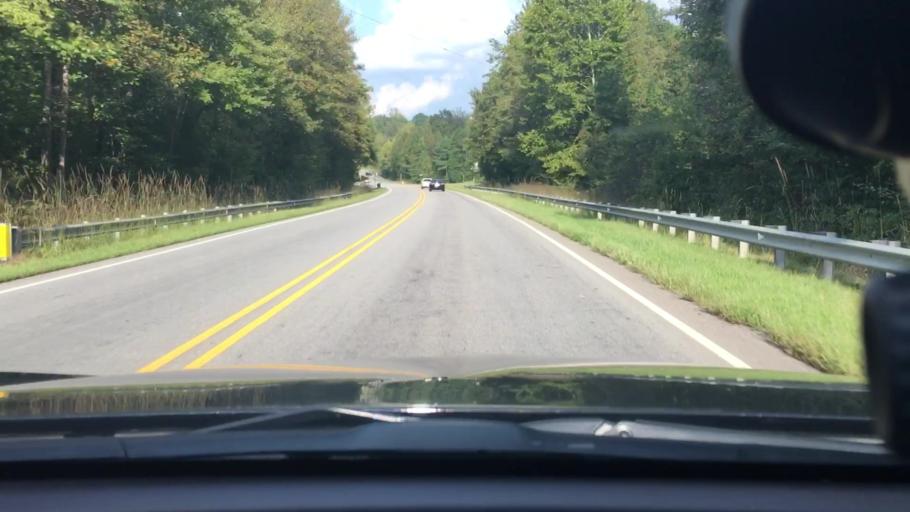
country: US
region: North Carolina
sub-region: Randolph County
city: Asheboro
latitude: 35.6671
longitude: -79.8834
